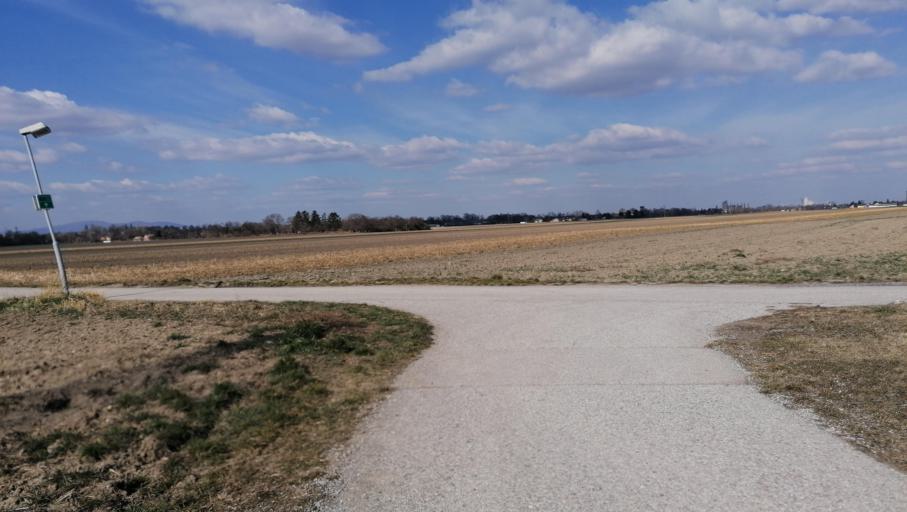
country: AT
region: Lower Austria
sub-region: Politischer Bezirk Wiener Neustadt
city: Lichtenworth
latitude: 47.8171
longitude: 16.2692
